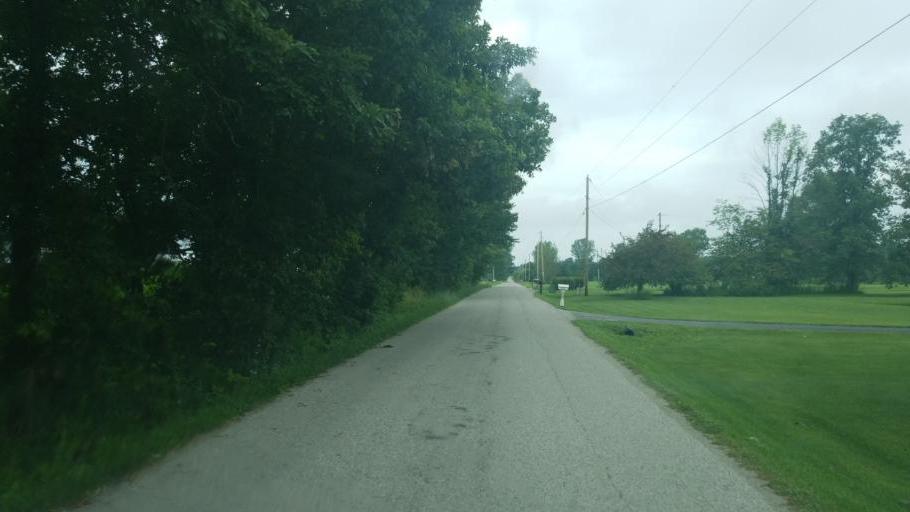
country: US
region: Ohio
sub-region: Knox County
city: Centerburg
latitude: 40.3813
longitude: -82.7745
